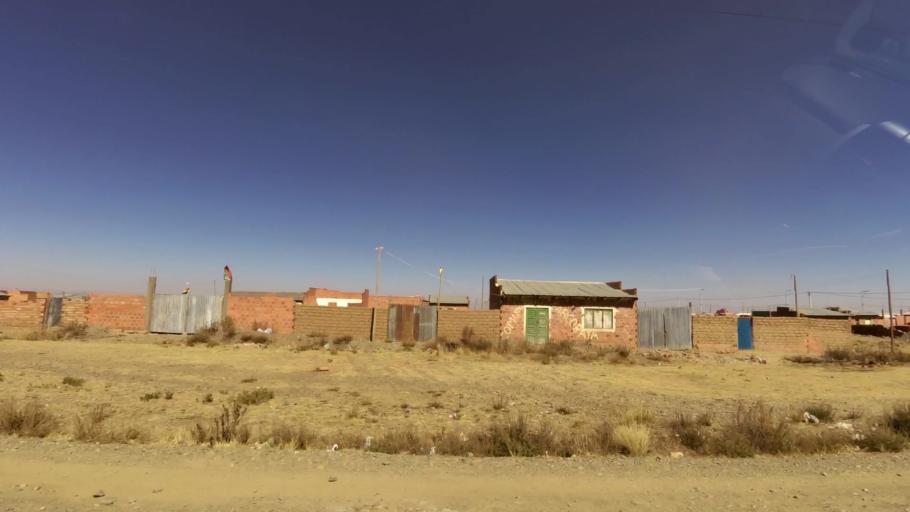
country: BO
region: La Paz
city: La Paz
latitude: -16.5842
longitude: -68.2133
